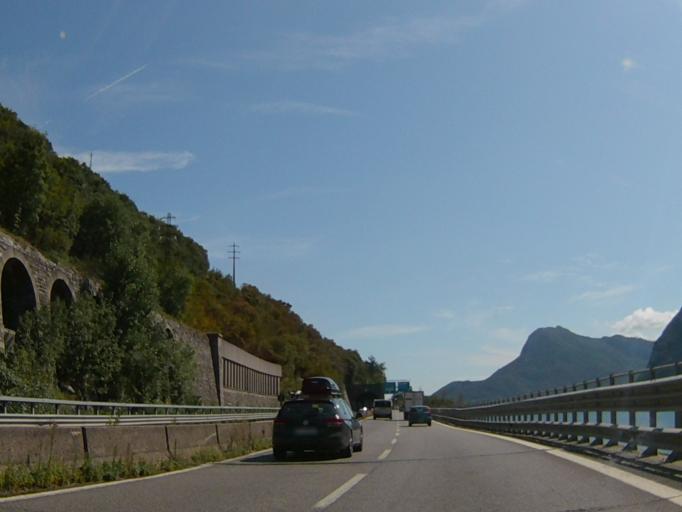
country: IT
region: Lombardy
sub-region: Provincia di Lecco
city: Abbadia Lariana
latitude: 45.8880
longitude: 9.3590
